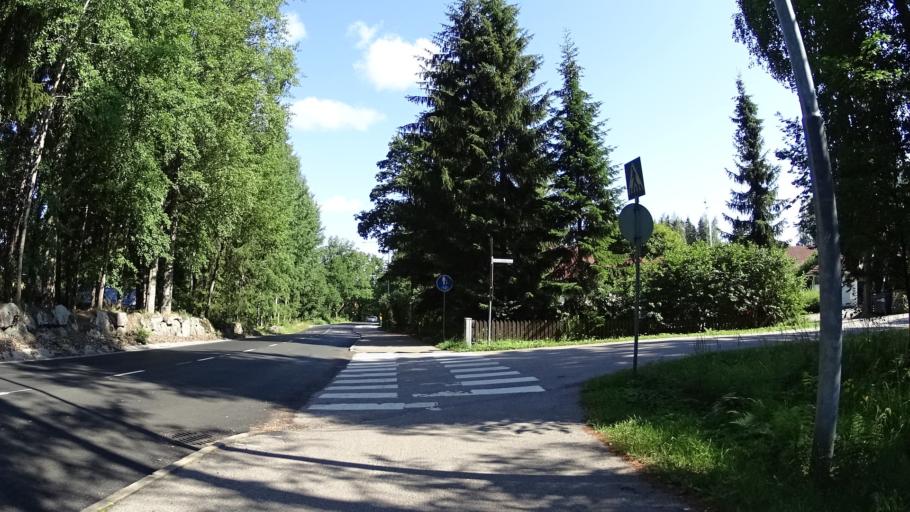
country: FI
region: Uusimaa
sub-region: Helsinki
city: Tuusula
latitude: 60.4093
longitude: 25.0297
